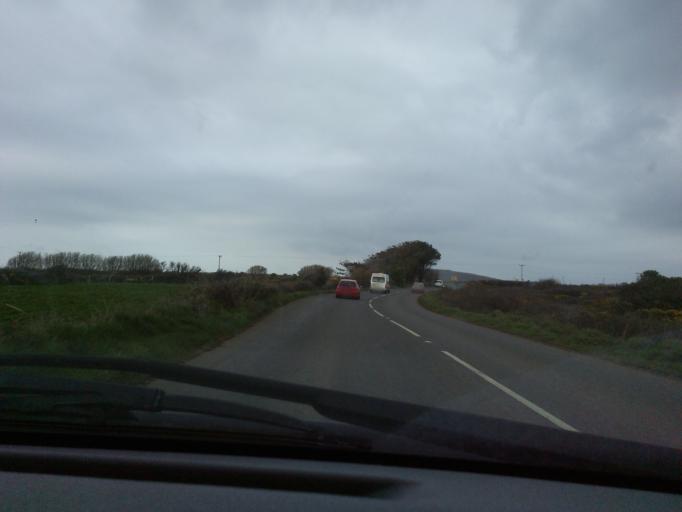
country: GB
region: England
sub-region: Cornwall
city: Sennen
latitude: 50.0857
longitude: -5.6754
